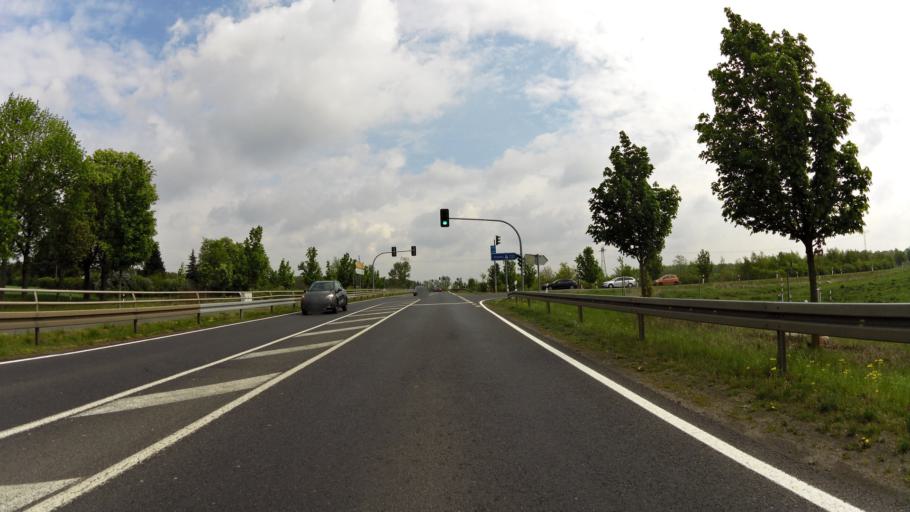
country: DE
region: Brandenburg
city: Mittenwalde
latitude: 52.2648
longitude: 13.5743
